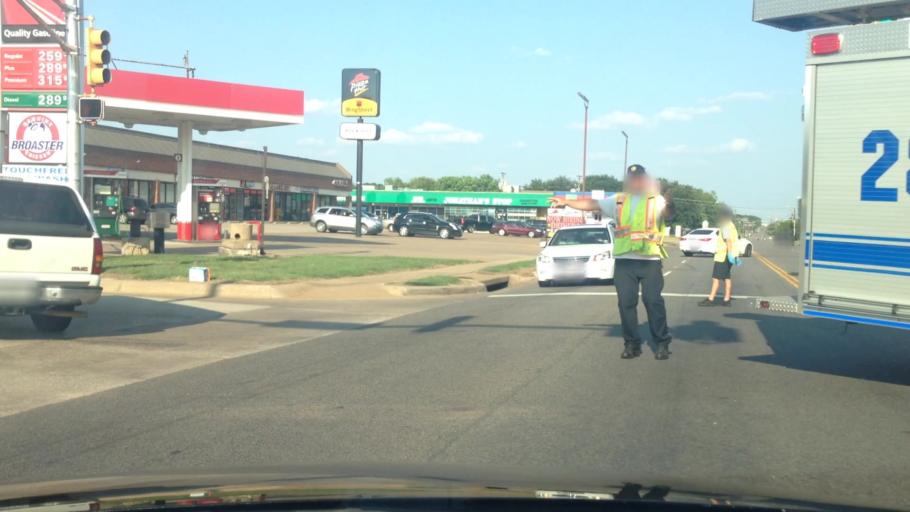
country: US
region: Texas
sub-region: Tarrant County
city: Edgecliff Village
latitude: 32.6352
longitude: -97.3397
